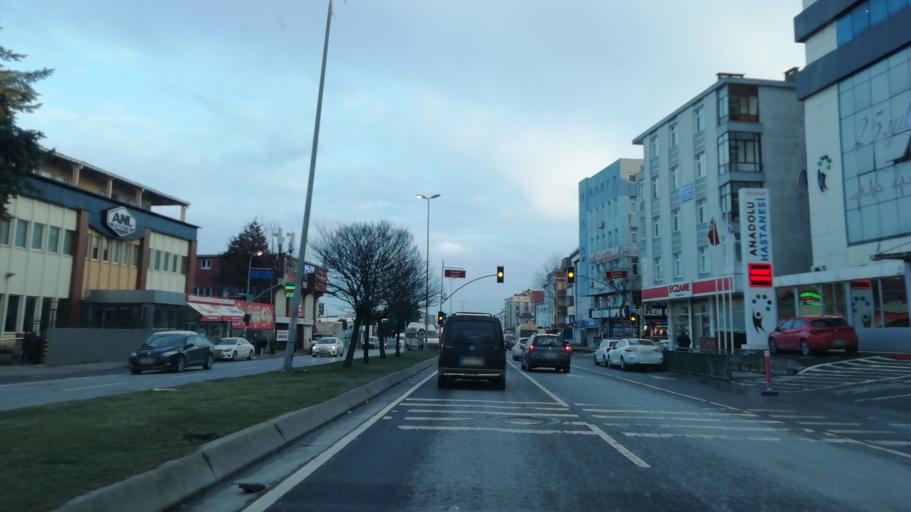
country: TR
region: Istanbul
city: Yakuplu
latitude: 41.0059
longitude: 28.7062
